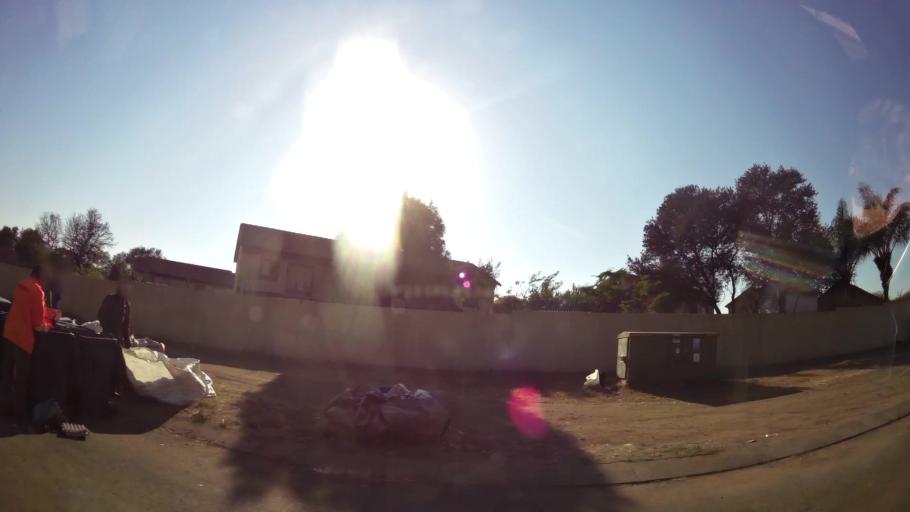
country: ZA
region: Gauteng
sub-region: City of Tshwane Metropolitan Municipality
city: Pretoria
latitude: -25.6709
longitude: 28.2122
